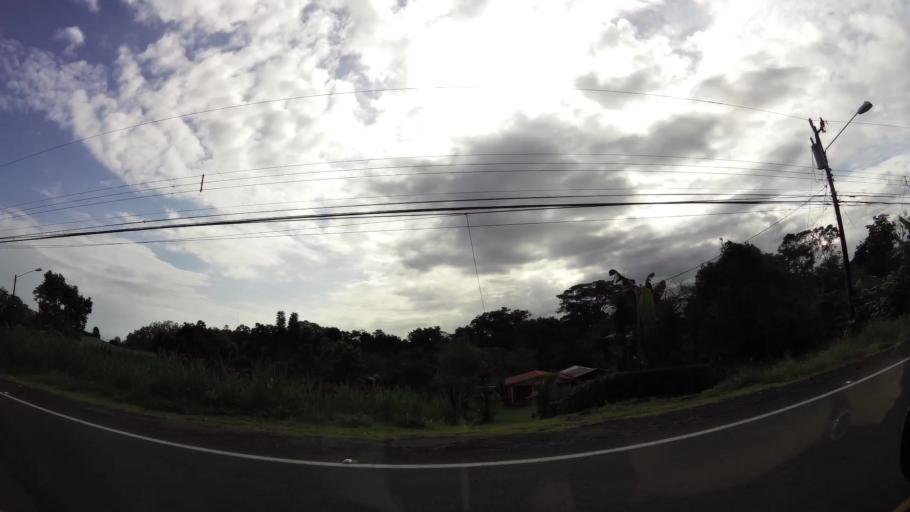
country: CR
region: Limon
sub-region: Canton de Guacimo
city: Guacimo
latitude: 10.2072
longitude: -83.6840
